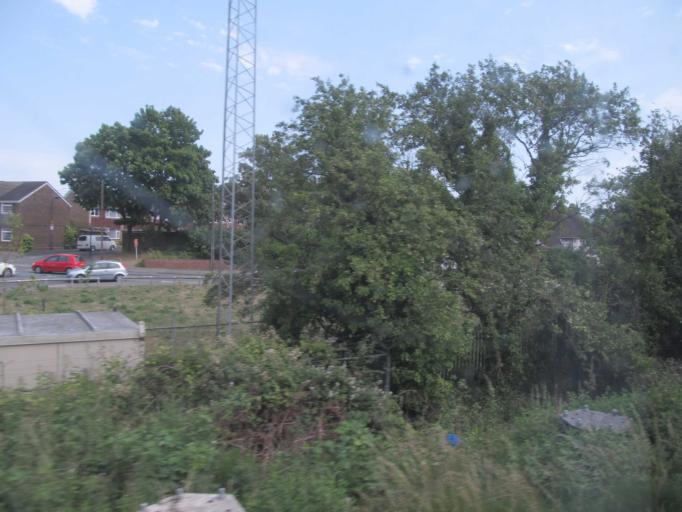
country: GB
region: England
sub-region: Buckinghamshire
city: Farnham Royal
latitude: 51.5235
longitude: -0.6459
